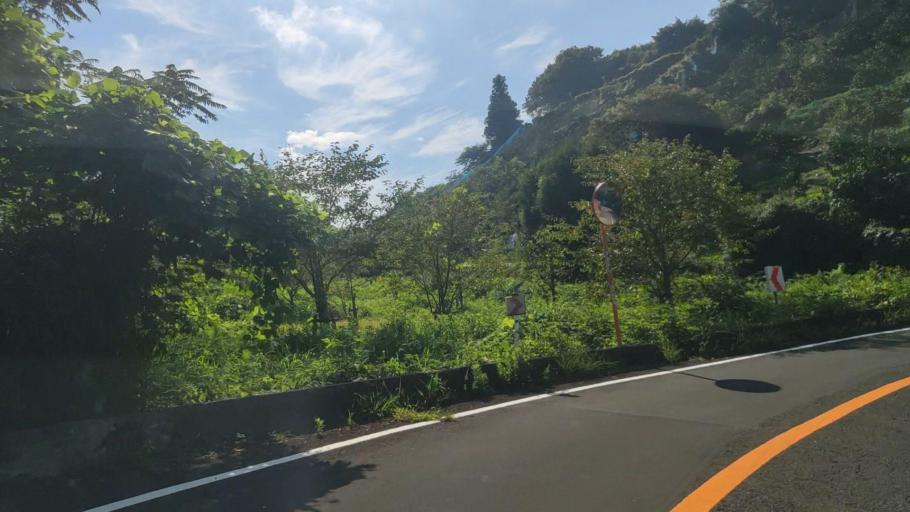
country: JP
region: Shizuoka
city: Shizuoka-shi
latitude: 34.9797
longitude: 138.4777
